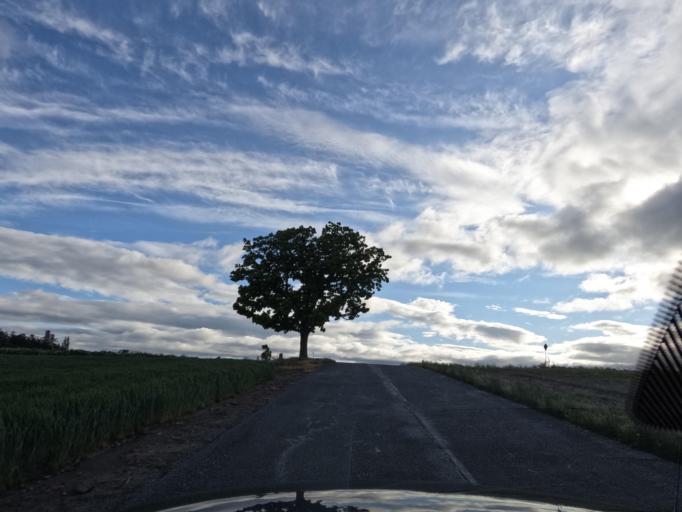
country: JP
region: Hokkaido
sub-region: Asahikawa-shi
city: Asahikawa
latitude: 43.6293
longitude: 142.4316
